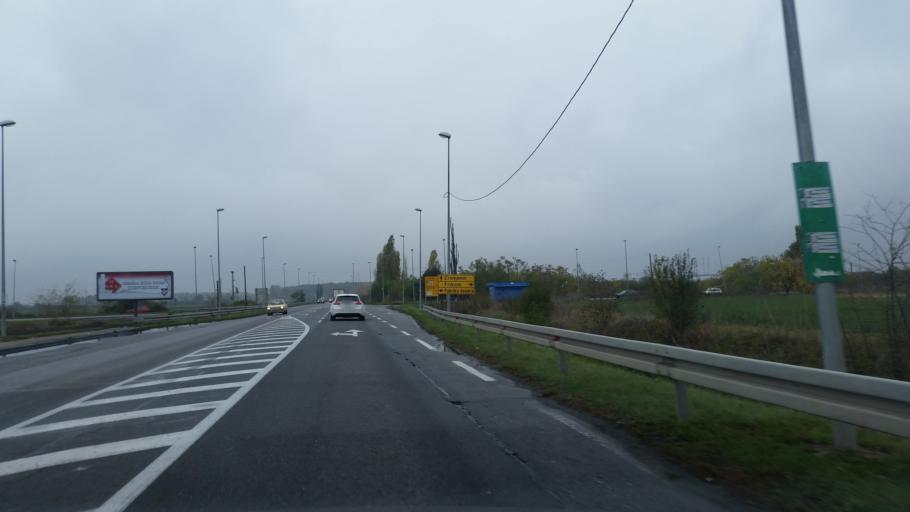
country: RS
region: Central Serbia
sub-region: Belgrade
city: Zemun
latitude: 44.9154
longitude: 20.4421
